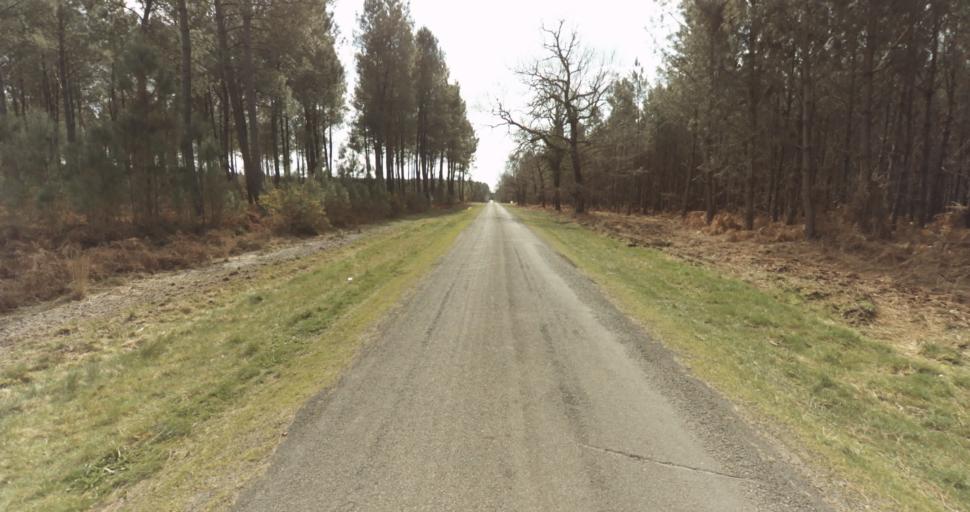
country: FR
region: Aquitaine
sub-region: Departement des Landes
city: Roquefort
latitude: 44.0558
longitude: -0.4287
